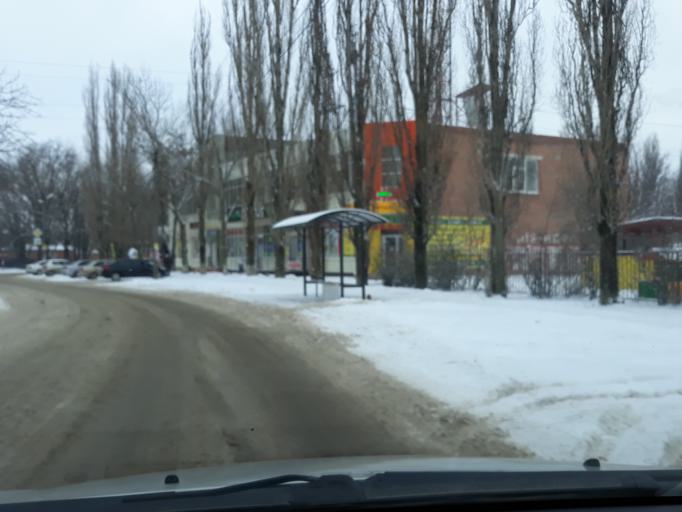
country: RU
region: Rostov
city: Taganrog
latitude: 47.2388
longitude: 38.8733
